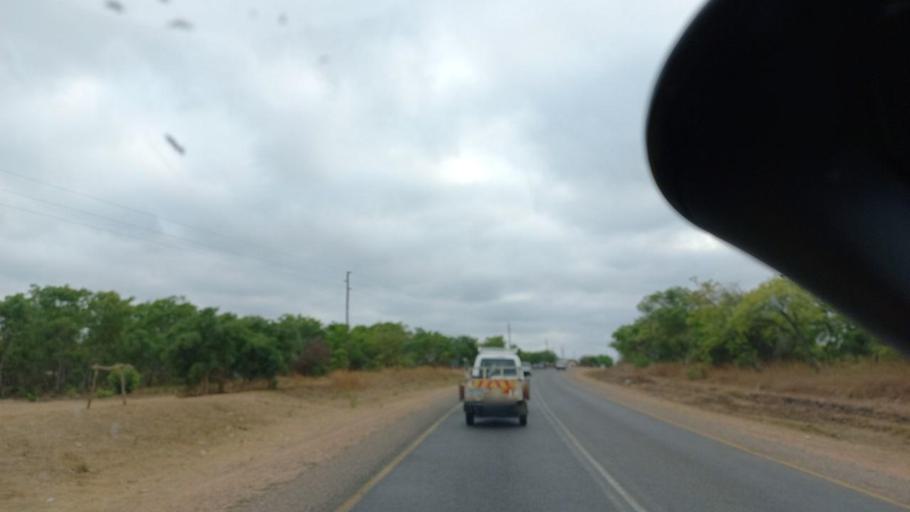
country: ZM
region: Lusaka
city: Chongwe
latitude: -15.2831
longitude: 28.7278
